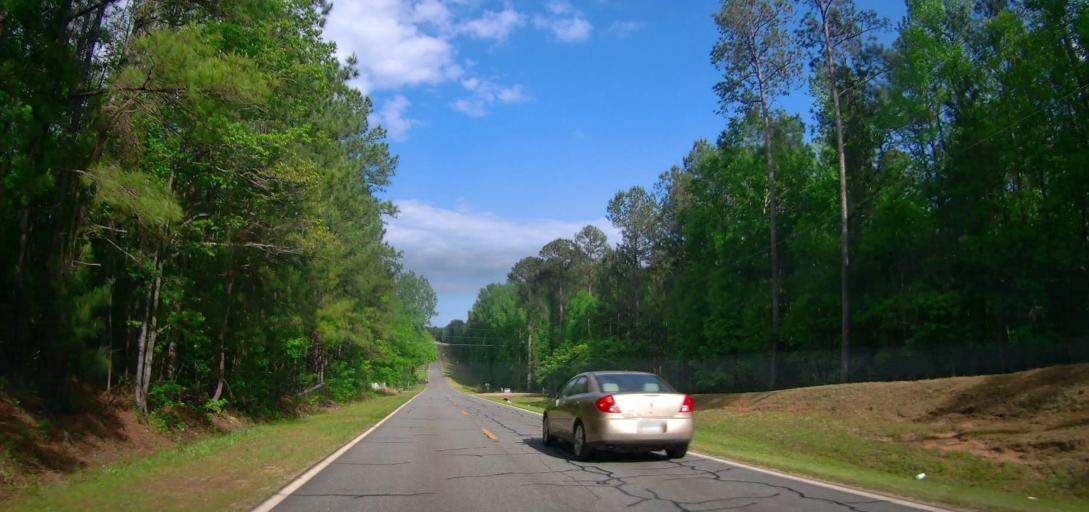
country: US
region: Georgia
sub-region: Baldwin County
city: Hardwick
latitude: 33.0632
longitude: -83.1616
